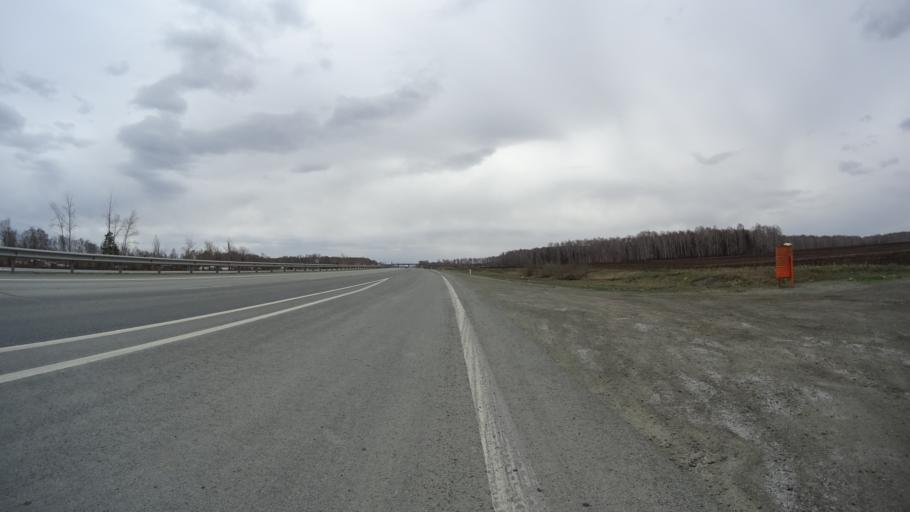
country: RU
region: Chelyabinsk
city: Yemanzhelinka
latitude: 54.8234
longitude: 61.3093
